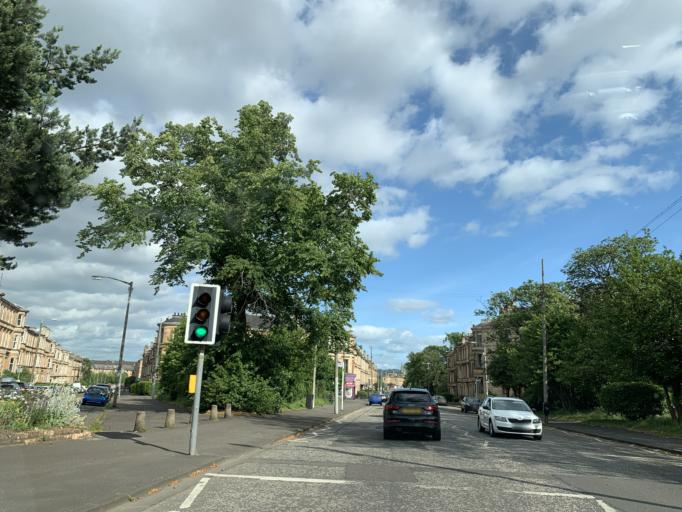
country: GB
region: Scotland
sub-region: Glasgow City
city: Glasgow
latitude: 55.8400
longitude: -4.2772
